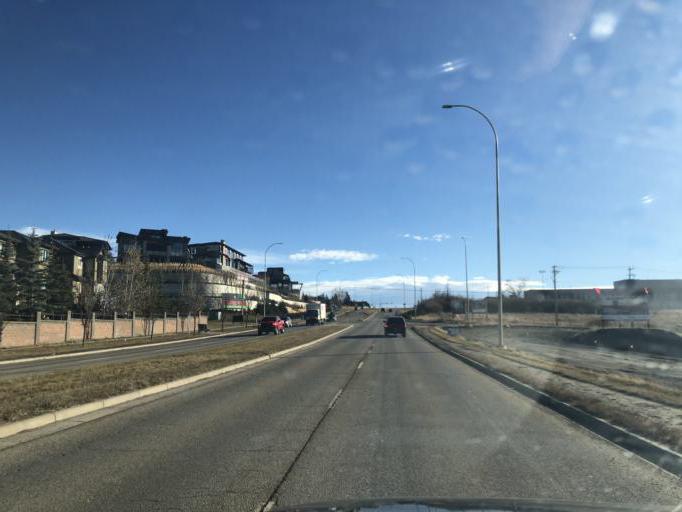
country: CA
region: Alberta
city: Calgary
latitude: 51.0379
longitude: -114.2011
